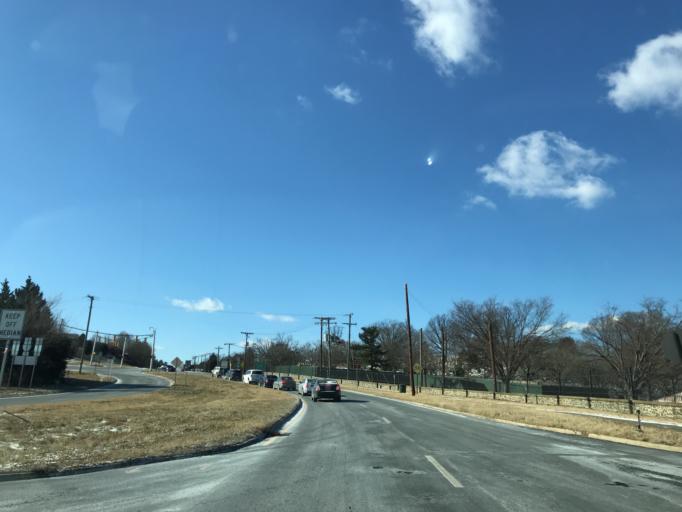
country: US
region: Washington, D.C.
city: Washington, D.C.
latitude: 38.8706
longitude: -77.0640
